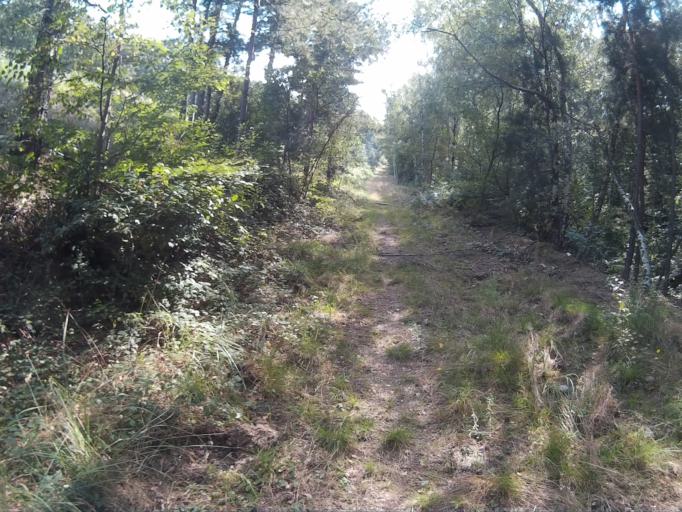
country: HU
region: Vas
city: Koszeg
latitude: 47.4002
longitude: 16.5109
